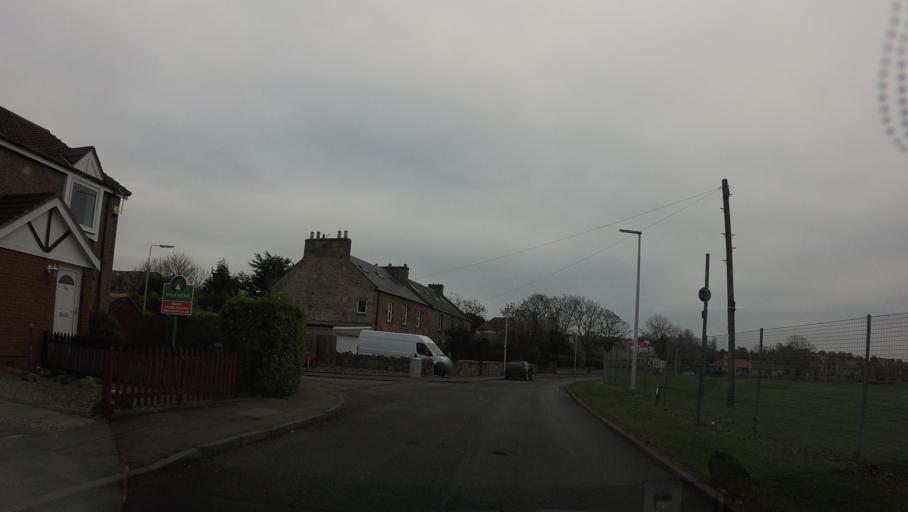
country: GB
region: Scotland
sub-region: Fife
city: Inverkeithing
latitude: 56.0288
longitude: -3.3912
